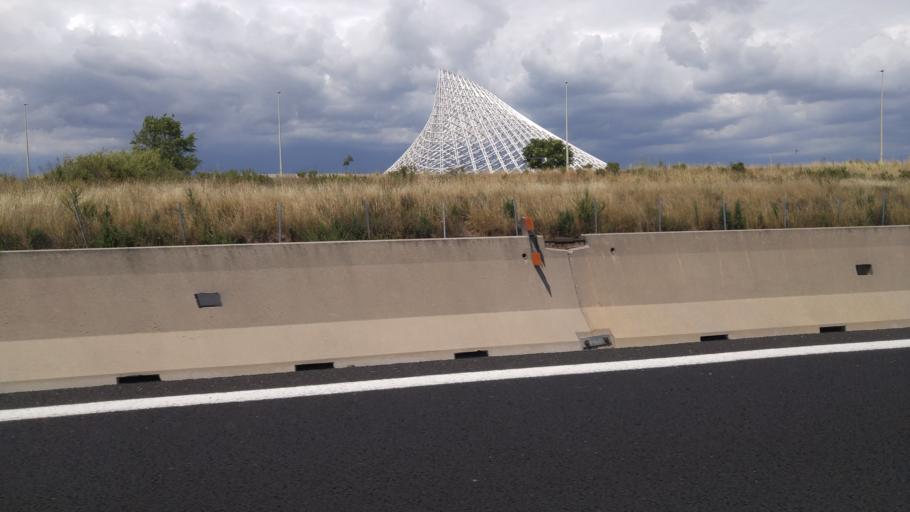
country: IT
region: Latium
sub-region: Citta metropolitana di Roma Capitale
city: Frascati
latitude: 41.8401
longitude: 12.6333
